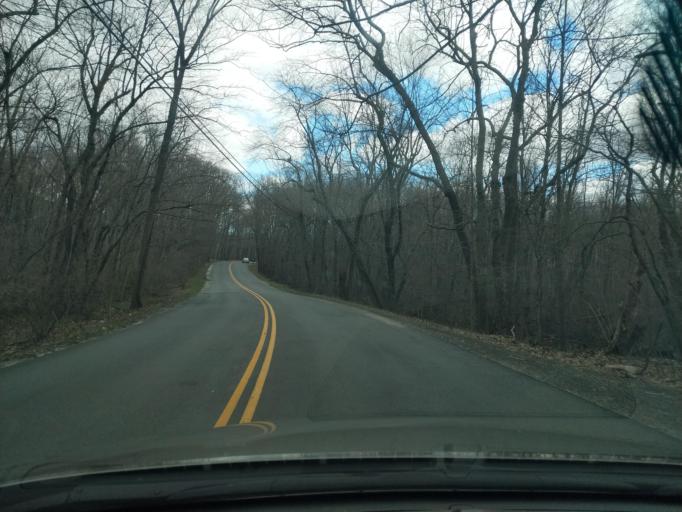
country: US
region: Connecticut
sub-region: Fairfield County
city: Newtown
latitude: 41.3557
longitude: -73.3239
